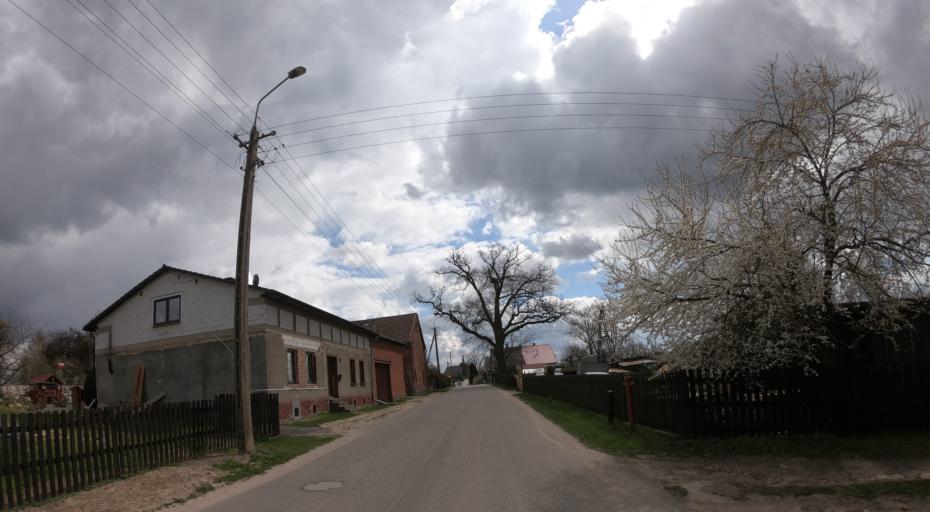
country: PL
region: West Pomeranian Voivodeship
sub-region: Powiat drawski
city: Drawsko Pomorskie
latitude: 53.5257
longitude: 15.8873
